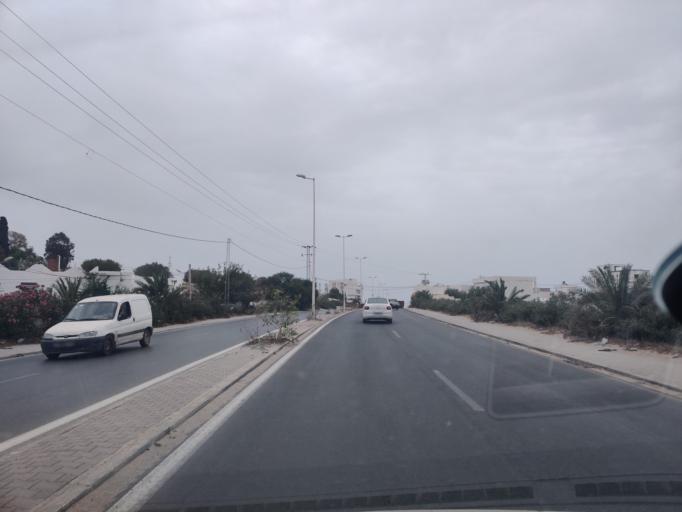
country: TN
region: Nabul
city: Al Hammamat
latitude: 36.4094
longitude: 10.6196
